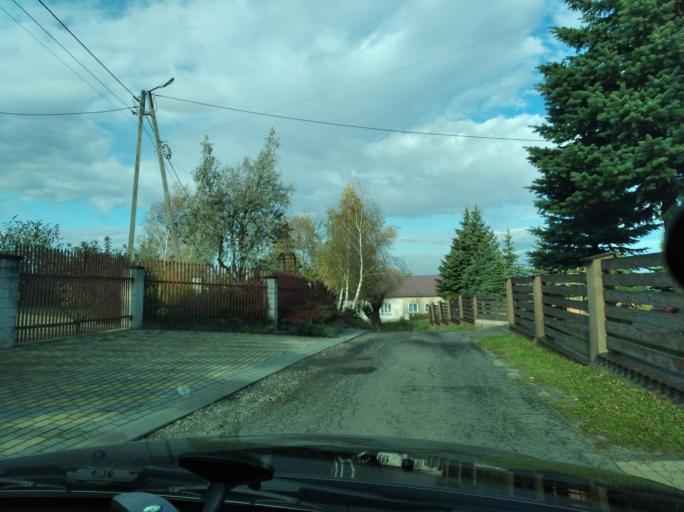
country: PL
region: Subcarpathian Voivodeship
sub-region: Powiat debicki
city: Debica
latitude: 50.0350
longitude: 21.4520
